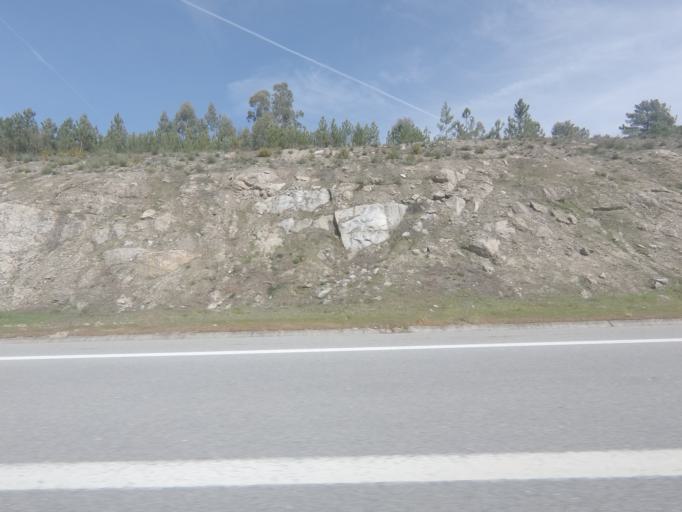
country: PT
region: Viseu
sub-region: Viseu
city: Viseu
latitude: 40.6329
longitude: -7.9760
